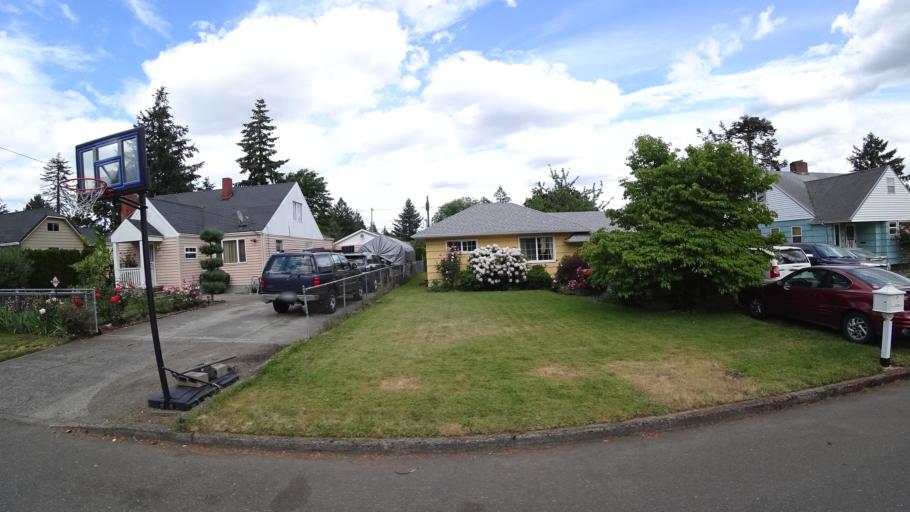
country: US
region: Oregon
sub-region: Multnomah County
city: Lents
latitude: 45.4985
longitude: -122.5493
